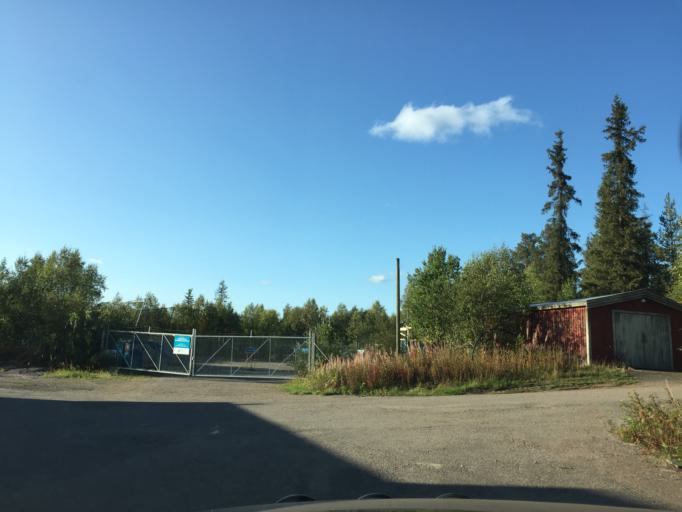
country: SE
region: Norrbotten
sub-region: Gallivare Kommun
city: Malmberget
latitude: 67.6538
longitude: 21.0372
